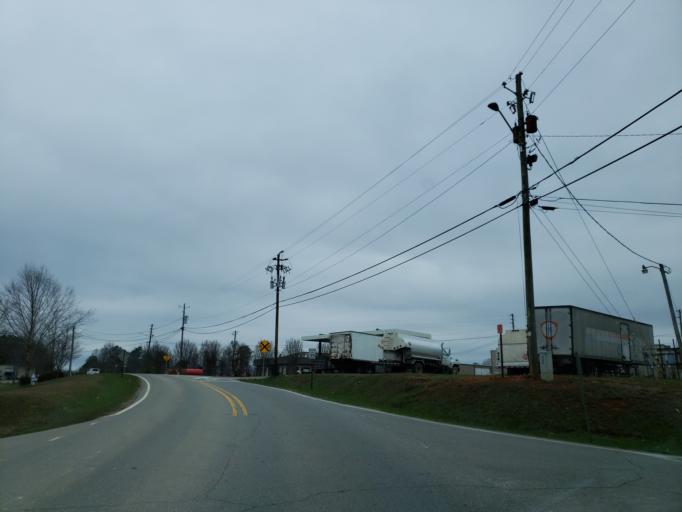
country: US
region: Georgia
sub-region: Pickens County
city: Jasper
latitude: 34.4736
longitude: -84.4372
